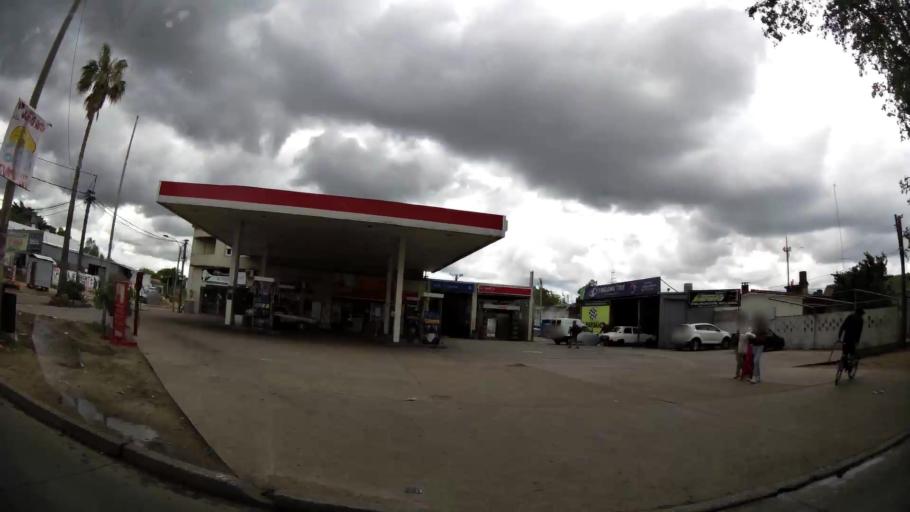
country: UY
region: Montevideo
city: Montevideo
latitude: -34.8244
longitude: -56.1406
